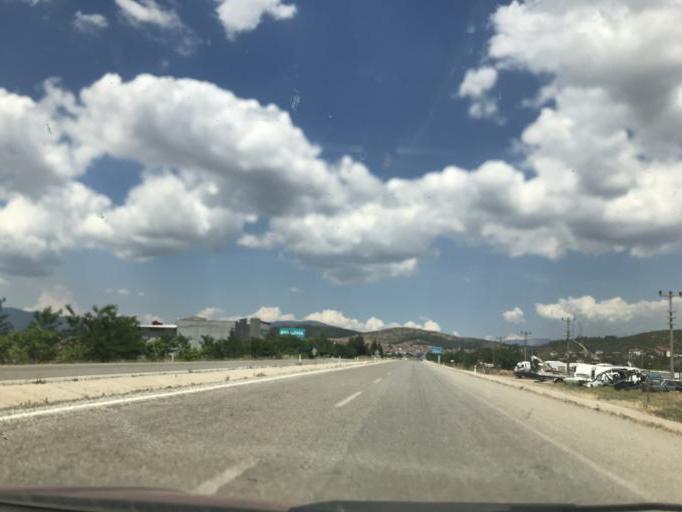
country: TR
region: Denizli
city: Tavas
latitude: 37.5544
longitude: 29.0543
